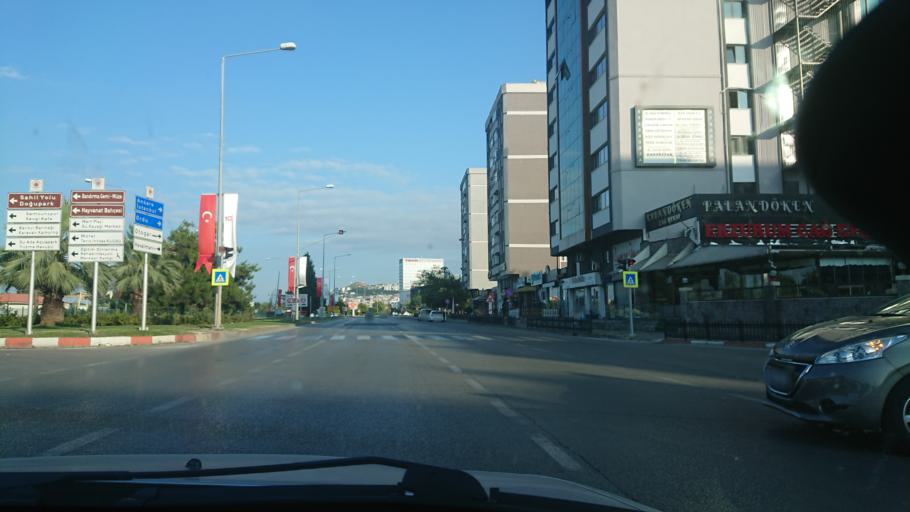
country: TR
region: Samsun
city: Samsun
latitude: 41.2804
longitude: 36.3489
